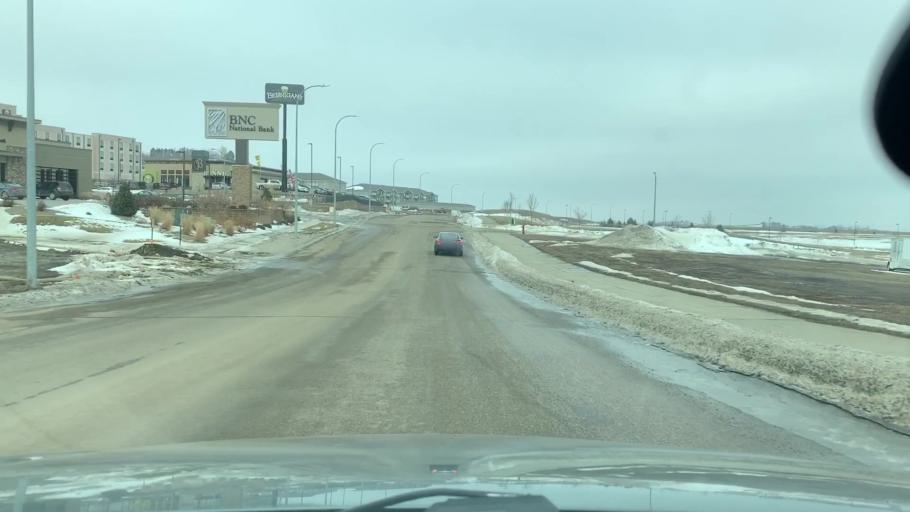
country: US
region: North Dakota
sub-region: Morton County
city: Mandan
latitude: 46.8494
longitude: -100.9092
